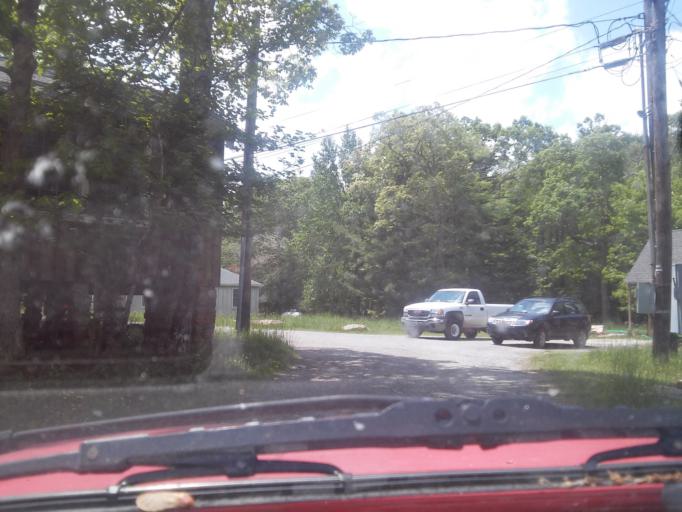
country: US
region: Virginia
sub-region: Giles County
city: Pembroke
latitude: 37.3759
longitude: -80.5241
